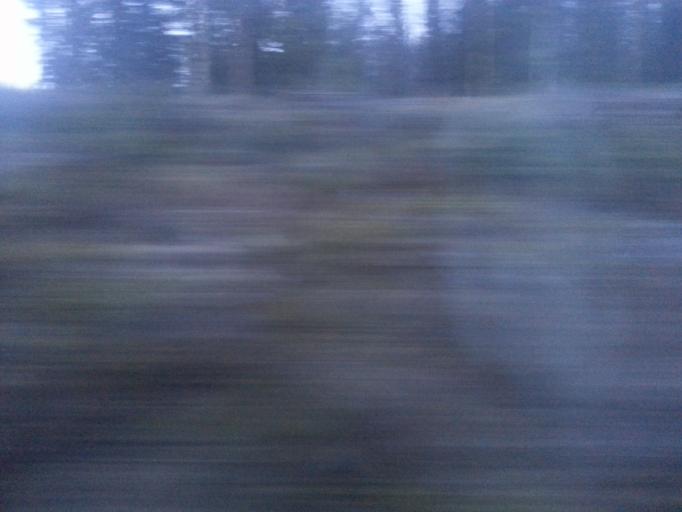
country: NO
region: Sor-Trondelag
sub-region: Rennebu
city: Berkak
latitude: 62.7105
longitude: 9.9634
